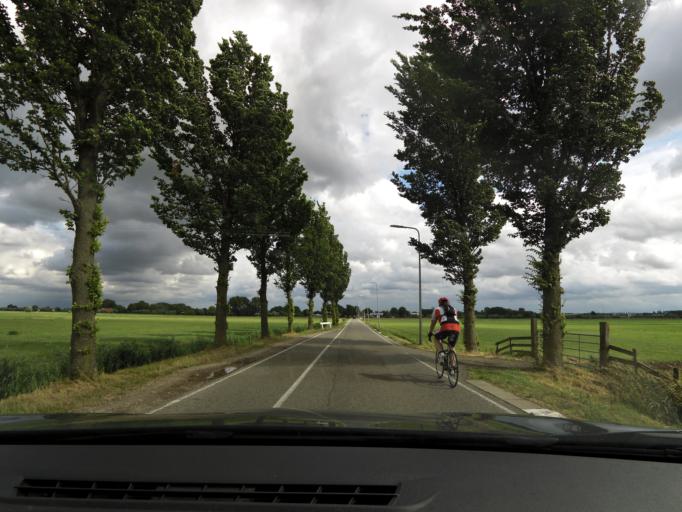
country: NL
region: South Holland
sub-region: Gemeente Vlaardingen
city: Vlaardingen
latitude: 51.9541
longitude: 4.3317
